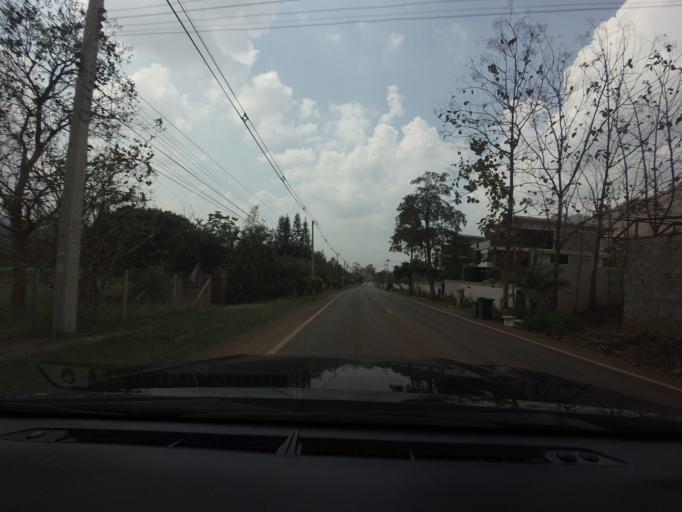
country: TH
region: Sara Buri
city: Muak Lek
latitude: 14.5779
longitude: 101.2674
